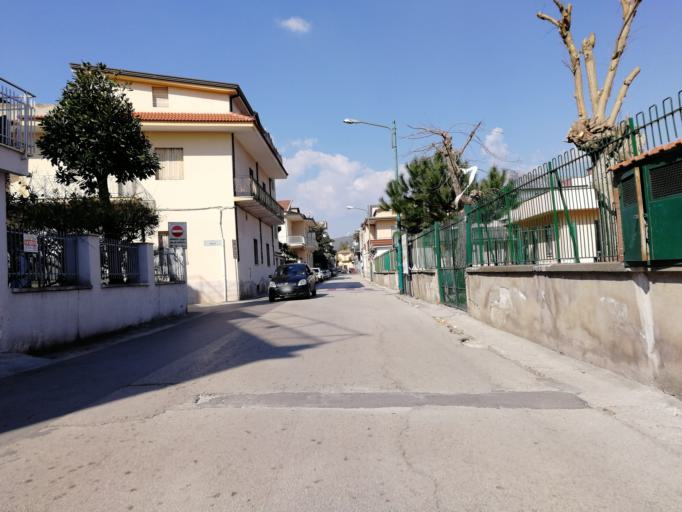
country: IT
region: Campania
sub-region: Provincia di Caserta
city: San Prisco
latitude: 41.0847
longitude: 14.2746
